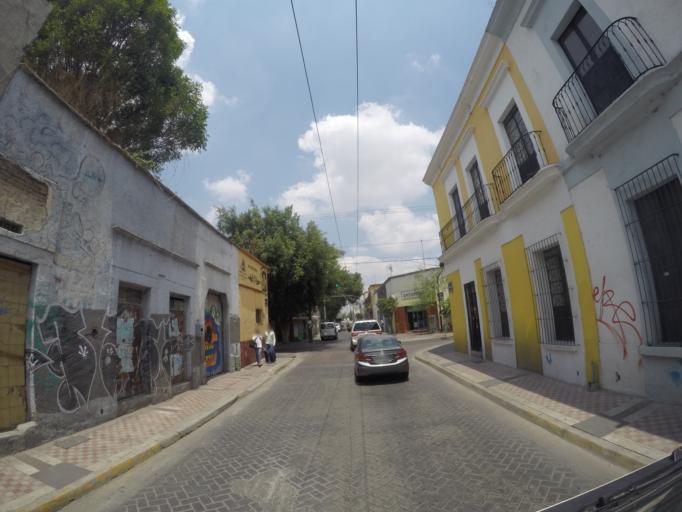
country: MX
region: Jalisco
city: Guadalajara
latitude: 20.6780
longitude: -103.3530
